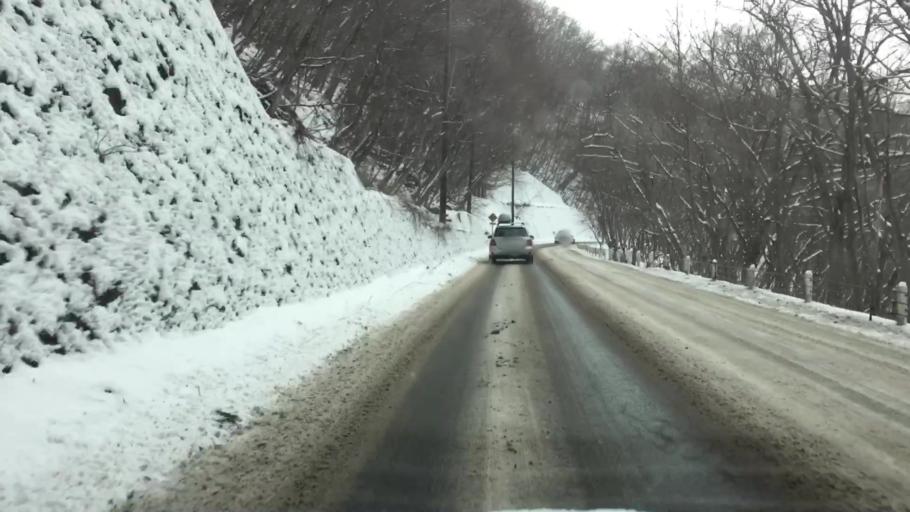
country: JP
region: Tochigi
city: Yaita
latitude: 36.9720
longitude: 139.7924
